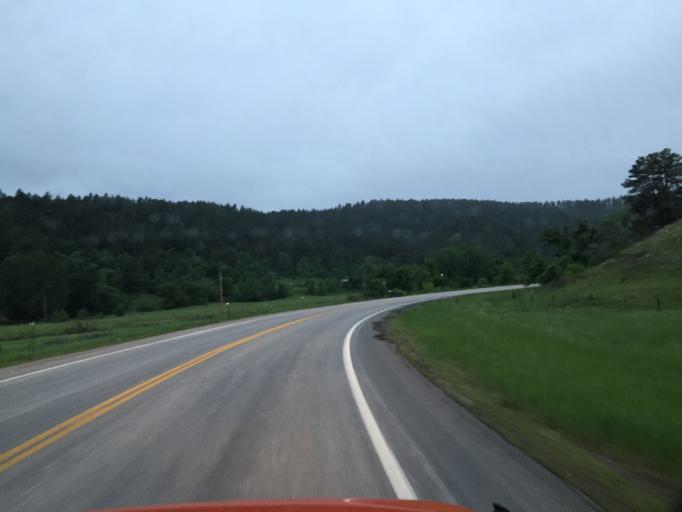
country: US
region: South Dakota
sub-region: Pennington County
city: Colonial Pine Hills
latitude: 43.8260
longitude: -103.2422
